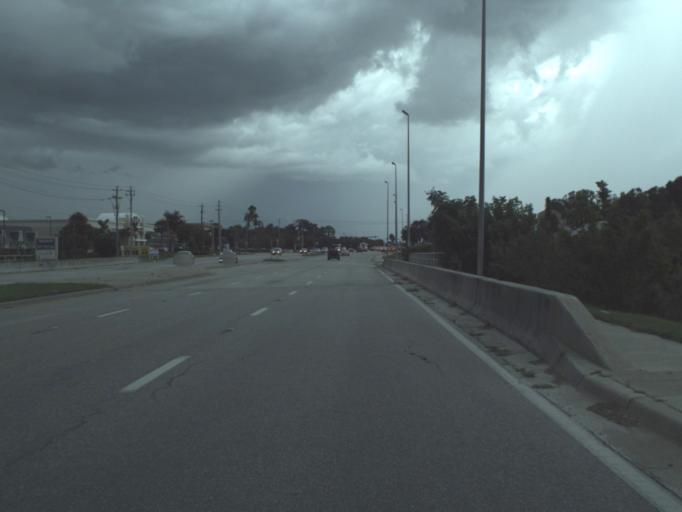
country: US
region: Florida
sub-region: Sarasota County
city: South Sarasota
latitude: 27.2754
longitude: -82.5305
